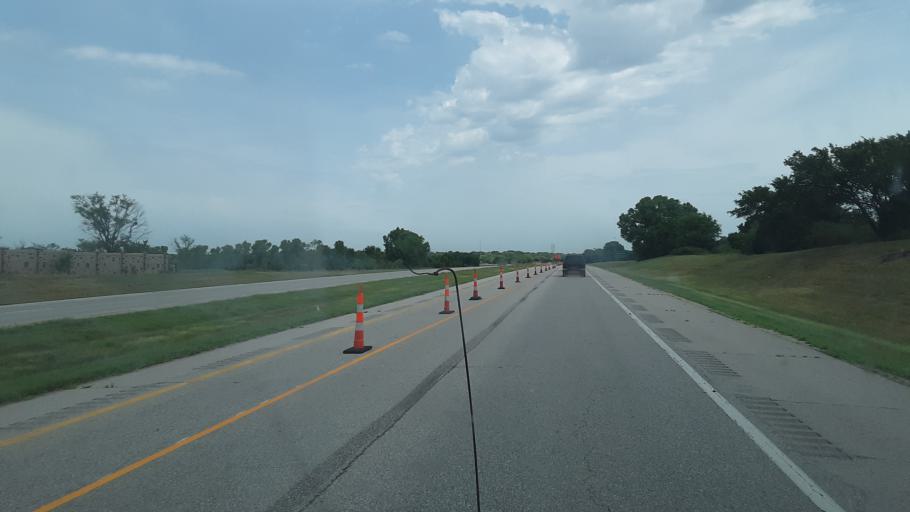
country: US
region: Kansas
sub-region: Sedgwick County
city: Kechi
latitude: 37.7820
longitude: -97.2868
